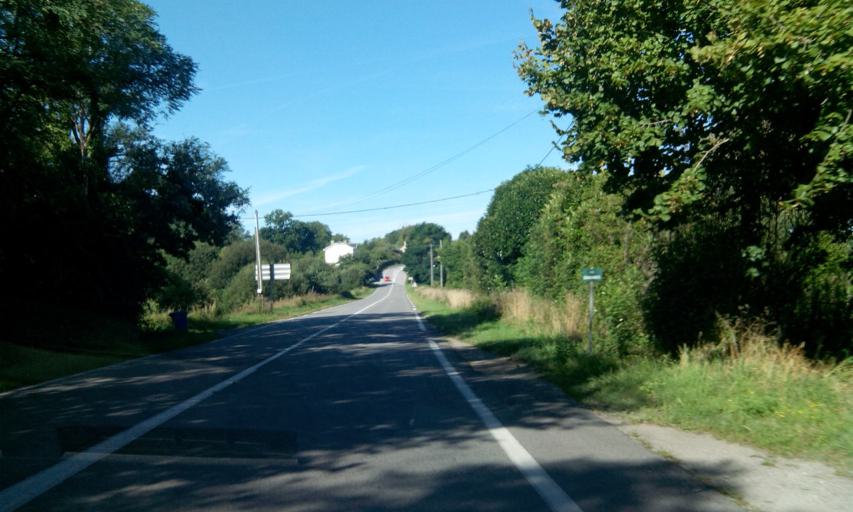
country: FR
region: Limousin
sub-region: Departement de la Haute-Vienne
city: Saint-Just-le-Martel
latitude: 45.8467
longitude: 1.3824
